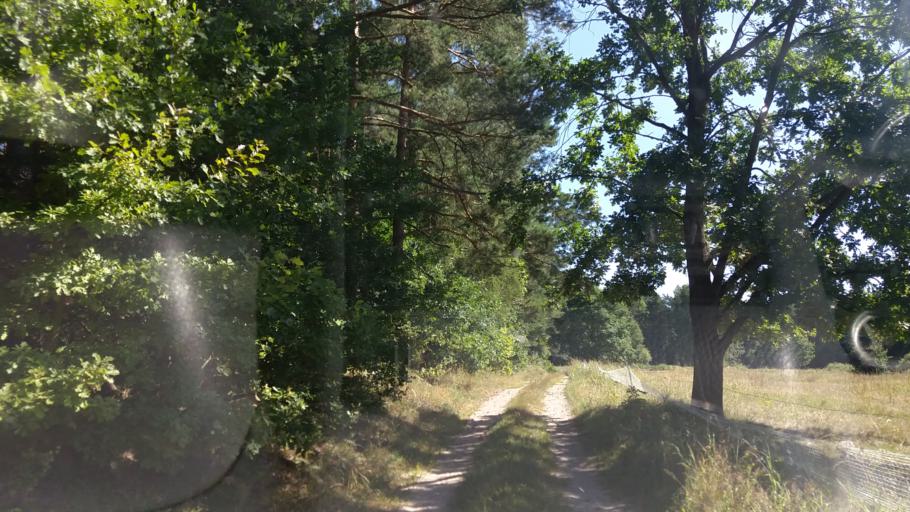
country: PL
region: West Pomeranian Voivodeship
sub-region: Powiat choszczenski
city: Krzecin
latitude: 53.0924
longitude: 15.4331
